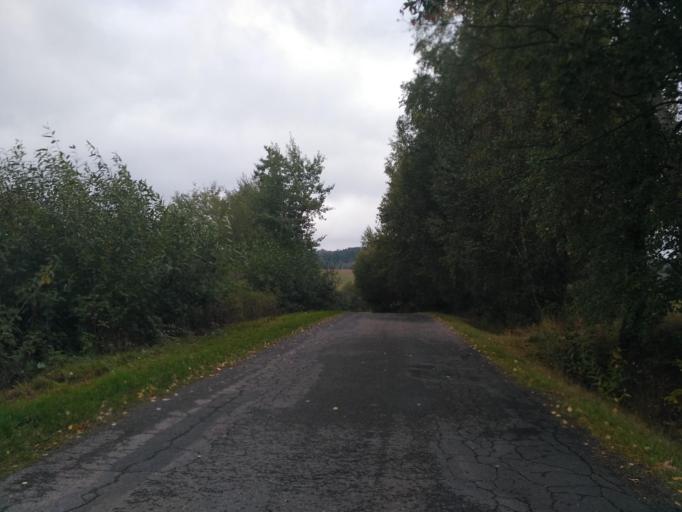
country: PL
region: Subcarpathian Voivodeship
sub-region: Powiat debicki
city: Brzostek
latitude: 49.9356
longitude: 21.4488
